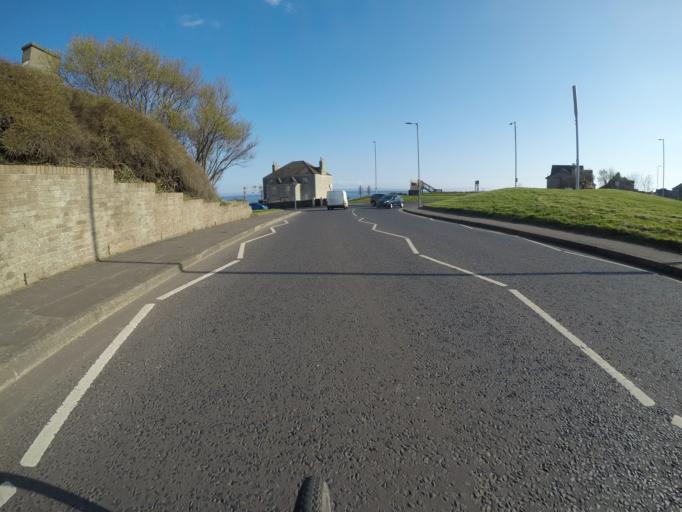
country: GB
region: Scotland
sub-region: North Ayrshire
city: Saltcoats
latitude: 55.6341
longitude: -4.7819
